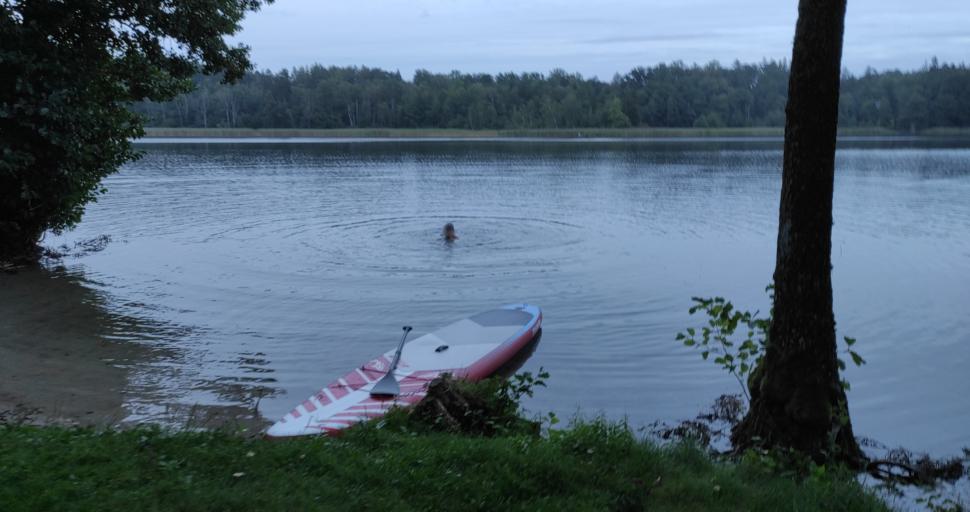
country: LV
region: Alsunga
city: Alsunga
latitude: 56.9340
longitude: 21.6496
